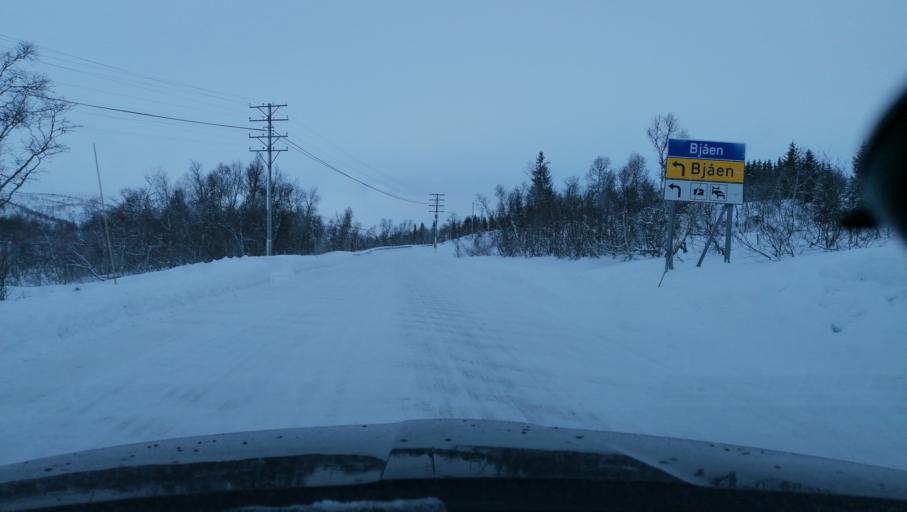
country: NO
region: Aust-Agder
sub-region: Bykle
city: Hovden
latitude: 59.6377
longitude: 7.4537
